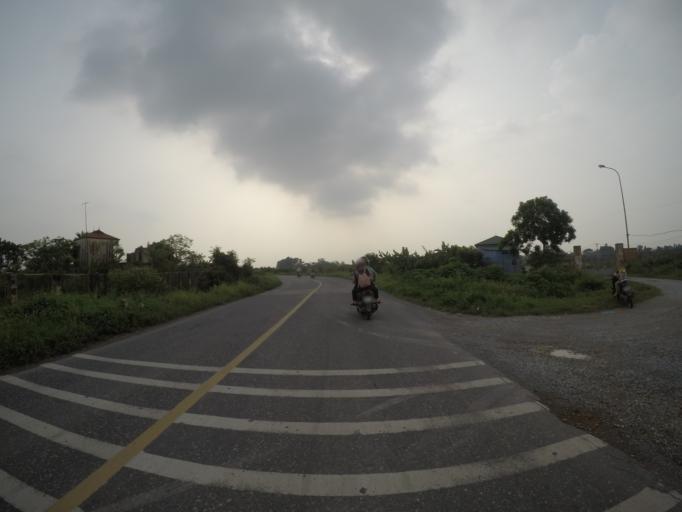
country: VN
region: Ha Noi
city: Soc Son
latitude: 21.2284
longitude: 105.7836
